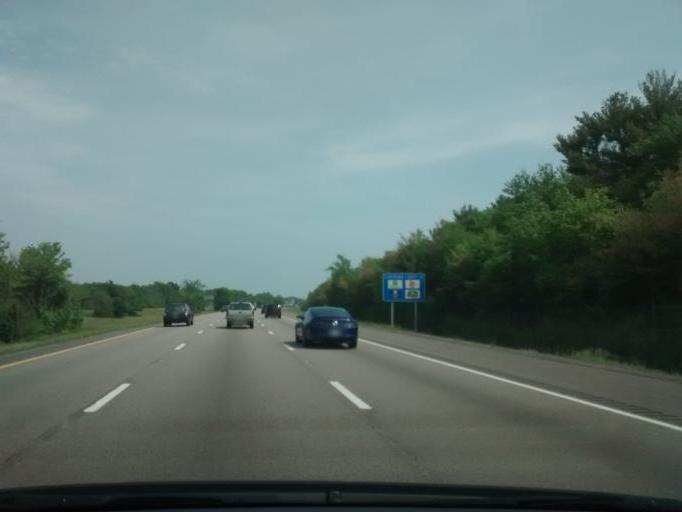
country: US
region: Massachusetts
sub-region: Bristol County
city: Mansfield Center
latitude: 42.0230
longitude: -71.2496
